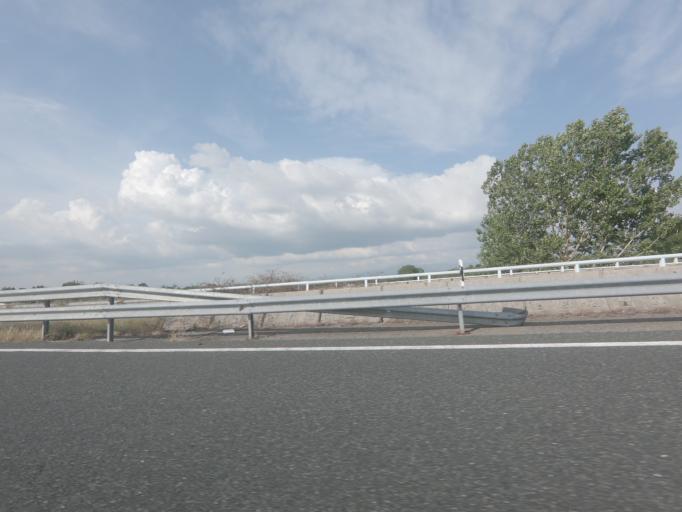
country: ES
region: Galicia
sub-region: Provincia de Ourense
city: Xinzo de Limia
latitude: 42.0997
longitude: -7.7297
